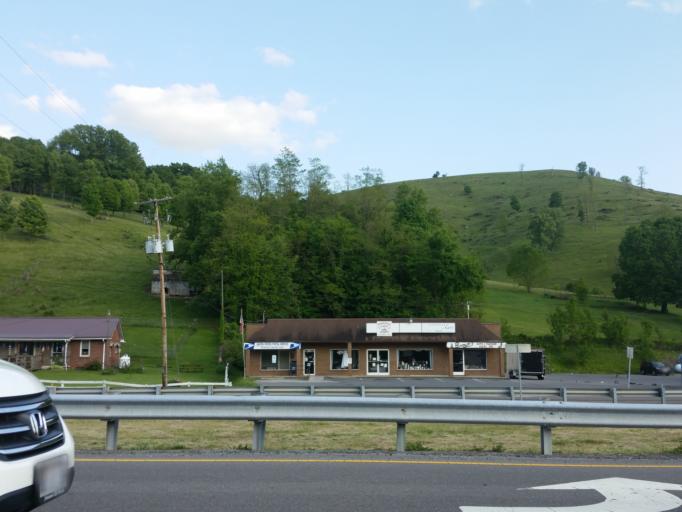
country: US
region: Virginia
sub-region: Russell County
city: Honaker
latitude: 36.9596
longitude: -81.9311
